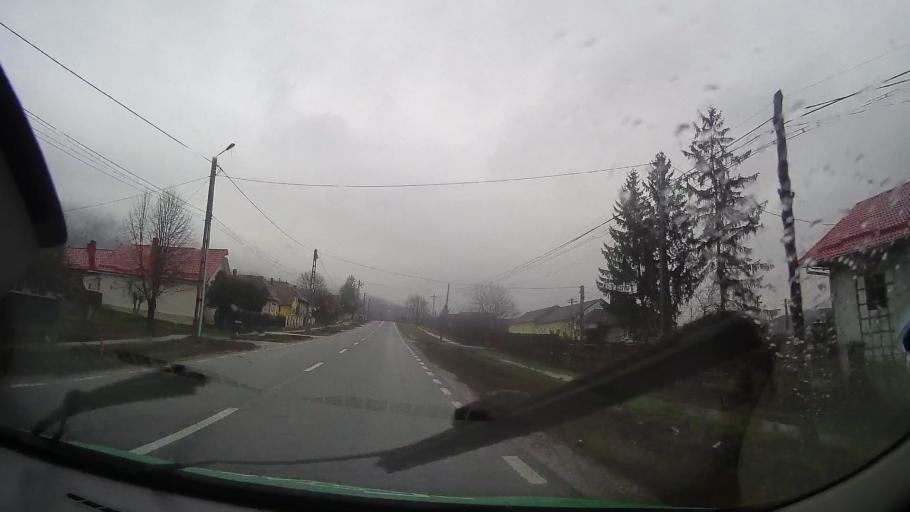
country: RO
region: Bistrita-Nasaud
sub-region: Comuna Galatii Bistritei
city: Galatii Bistritei
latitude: 46.9964
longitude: 24.4135
